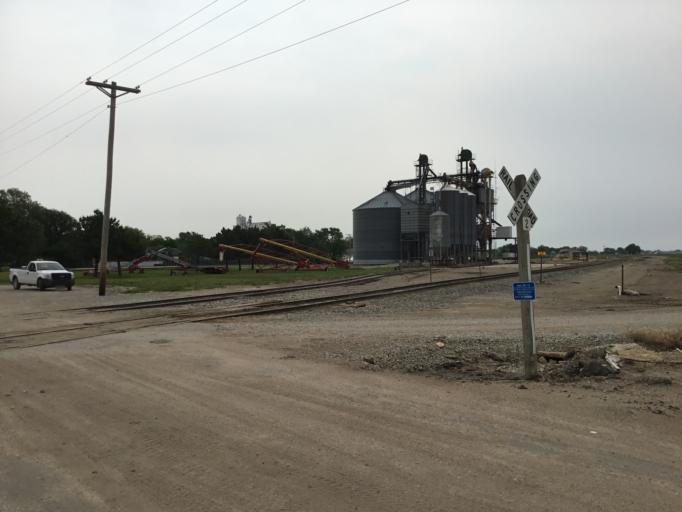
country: US
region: Kansas
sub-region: Republic County
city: Belleville
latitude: 39.7844
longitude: -97.9018
